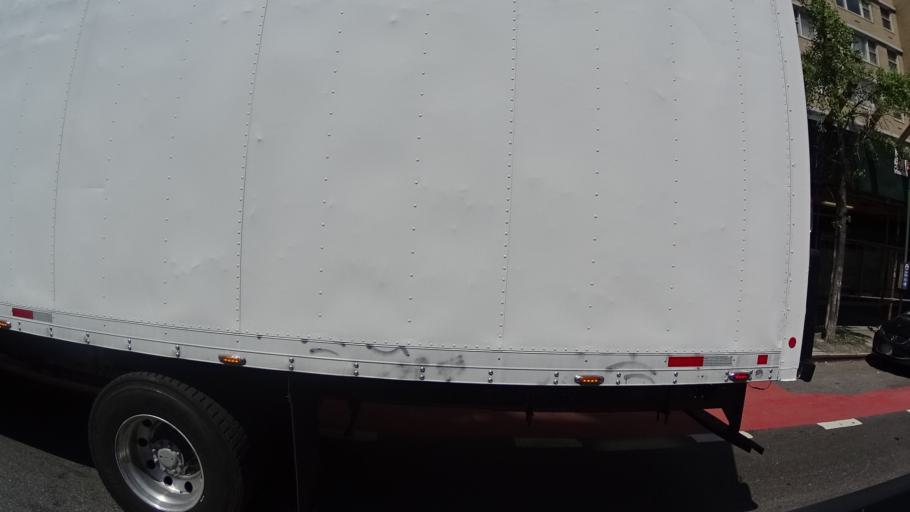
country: US
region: New York
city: New York City
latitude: 40.7356
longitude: -73.9826
